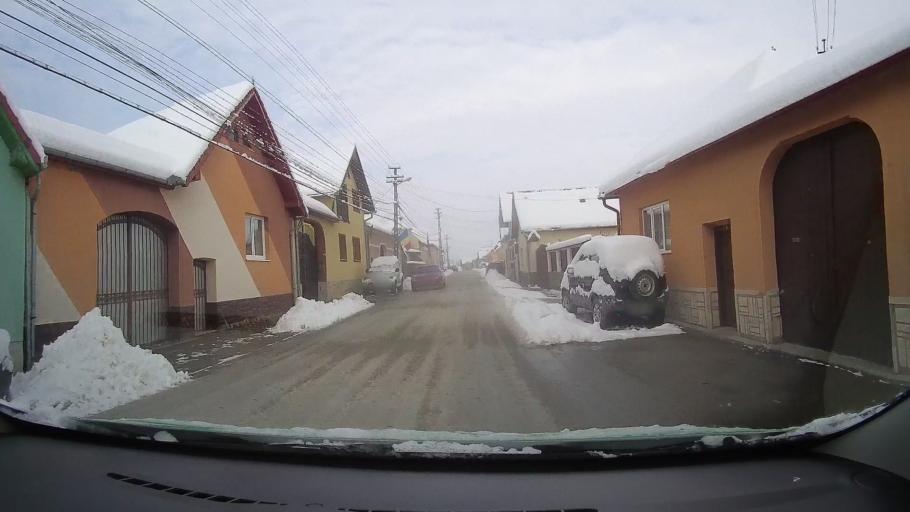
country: RO
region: Alba
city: Pianu de Sus
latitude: 45.8970
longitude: 23.4817
